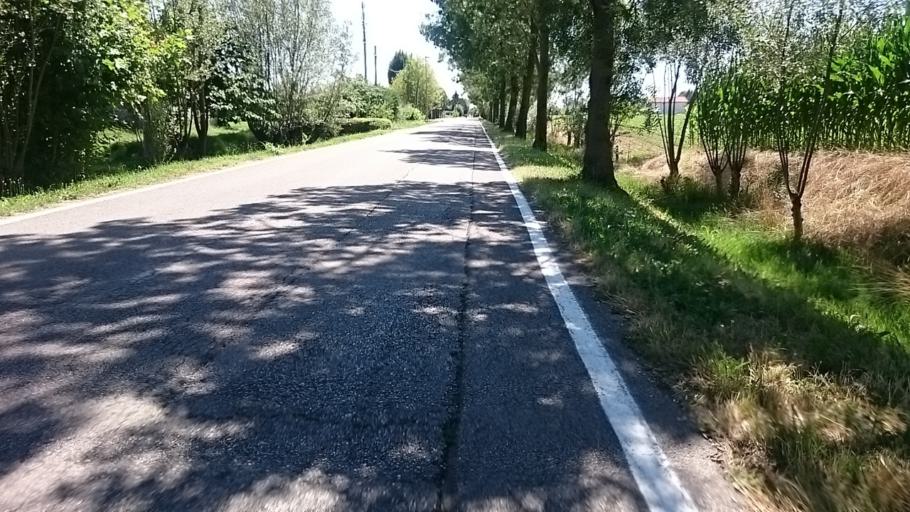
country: IT
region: Veneto
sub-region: Provincia di Padova
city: Villanova
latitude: 45.4861
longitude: 11.9761
